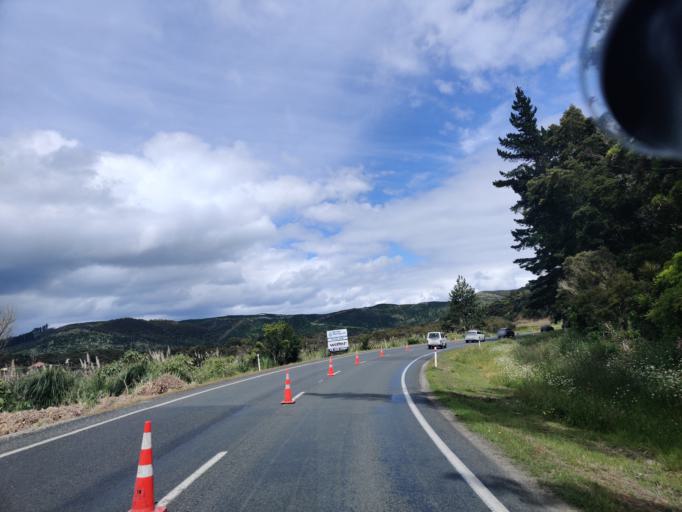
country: NZ
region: Northland
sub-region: Far North District
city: Taipa
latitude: -35.0121
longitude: 173.5540
